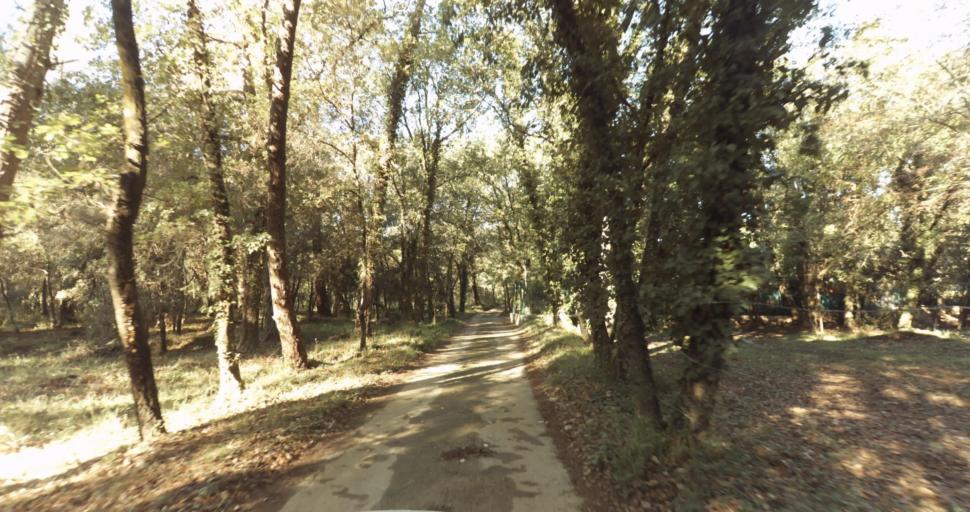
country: FR
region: Provence-Alpes-Cote d'Azur
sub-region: Departement des Alpes-Maritimes
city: Vence
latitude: 43.7100
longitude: 7.1035
